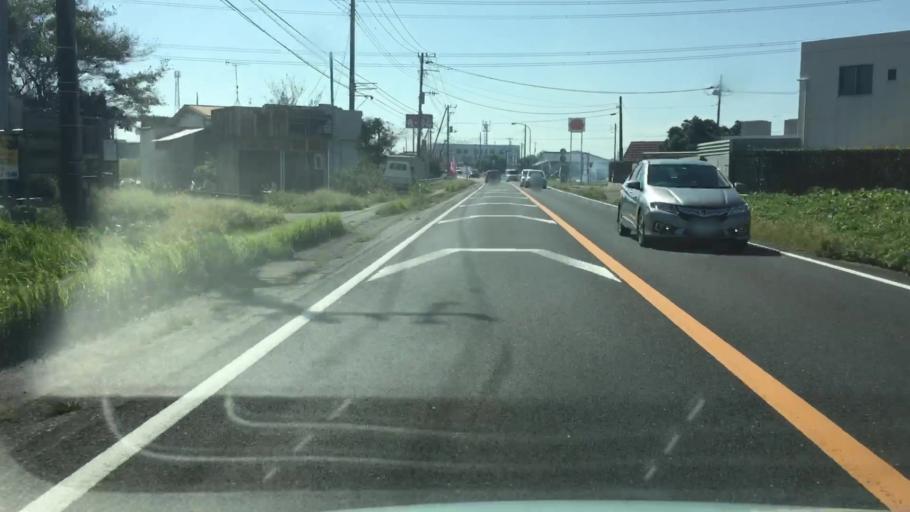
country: JP
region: Ibaraki
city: Ryugasaki
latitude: 35.8689
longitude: 140.1539
